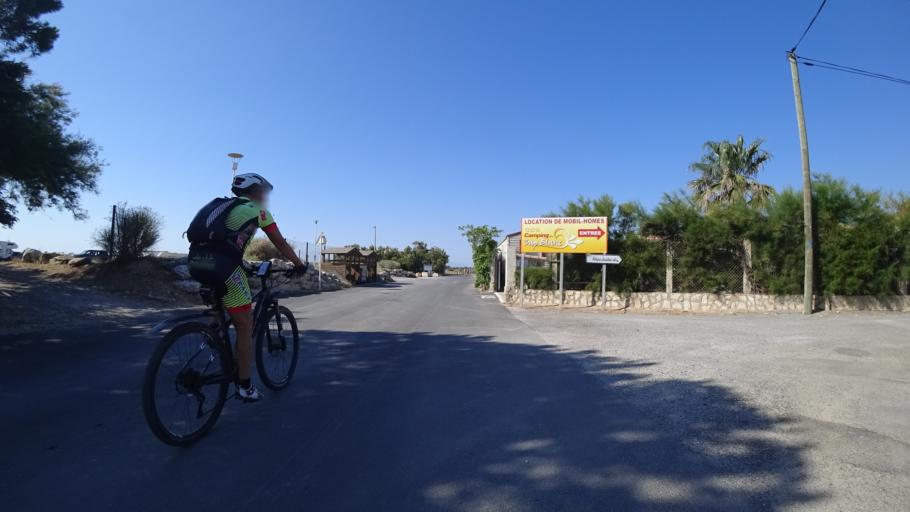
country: FR
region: Languedoc-Roussillon
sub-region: Departement de l'Aude
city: Leucate
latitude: 42.9006
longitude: 3.0529
